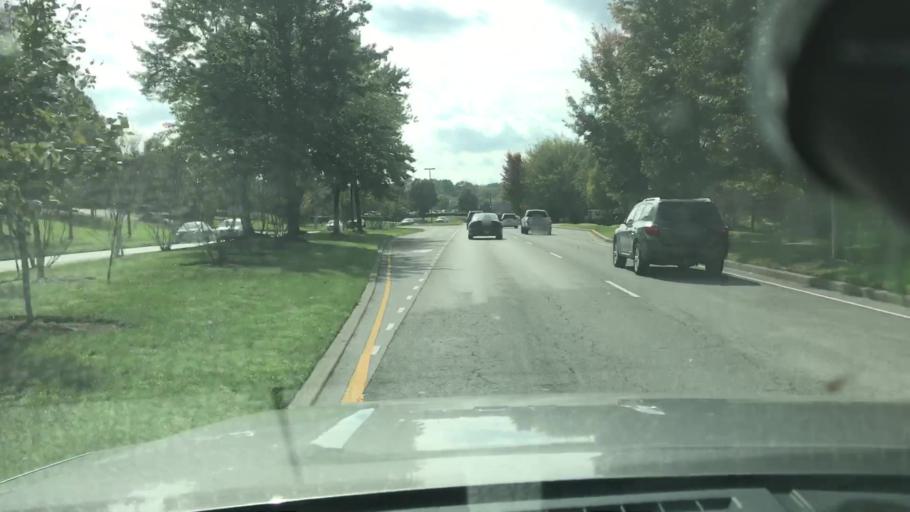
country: US
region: Tennessee
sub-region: Williamson County
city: Franklin
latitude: 35.9429
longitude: -86.8298
